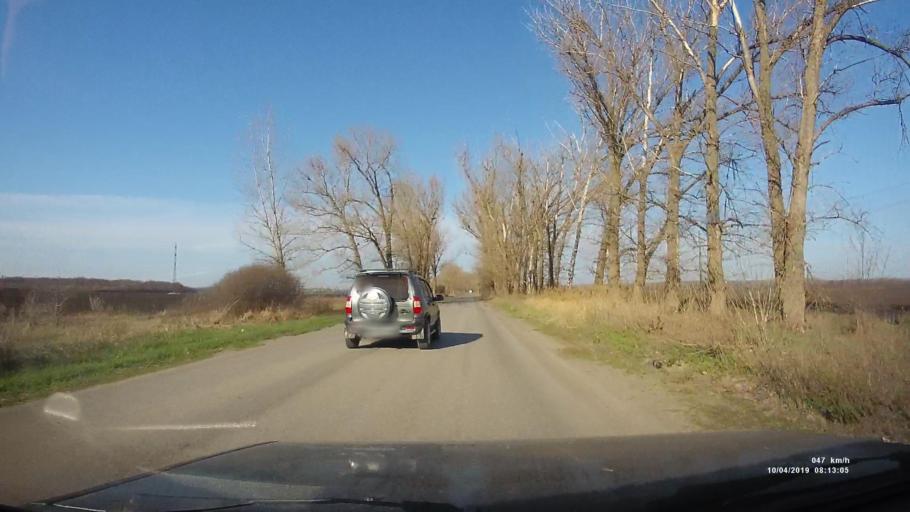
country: RU
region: Rostov
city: Masalovka
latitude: 48.3617
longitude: 40.2504
